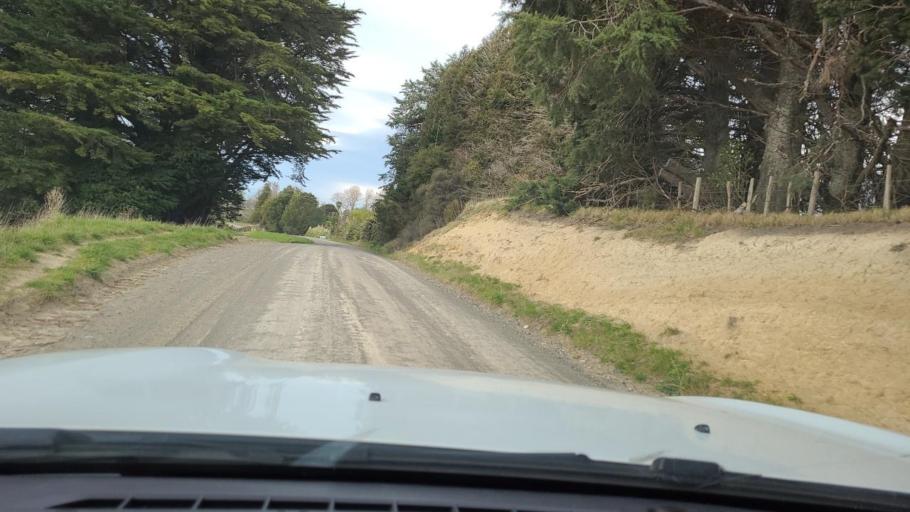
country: NZ
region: Hawke's Bay
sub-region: Napier City
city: Napier
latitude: -39.3220
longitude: 176.8359
